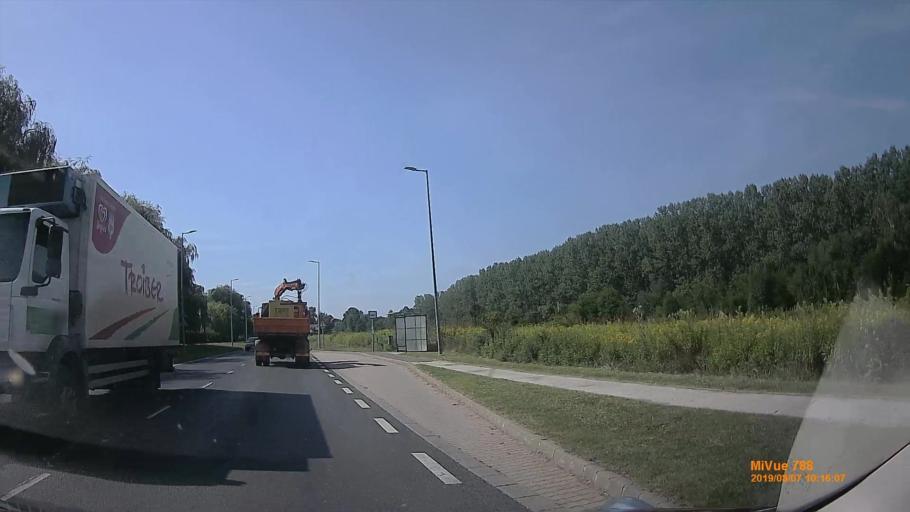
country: HU
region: Veszprem
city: Ajka
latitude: 47.1322
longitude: 17.5463
